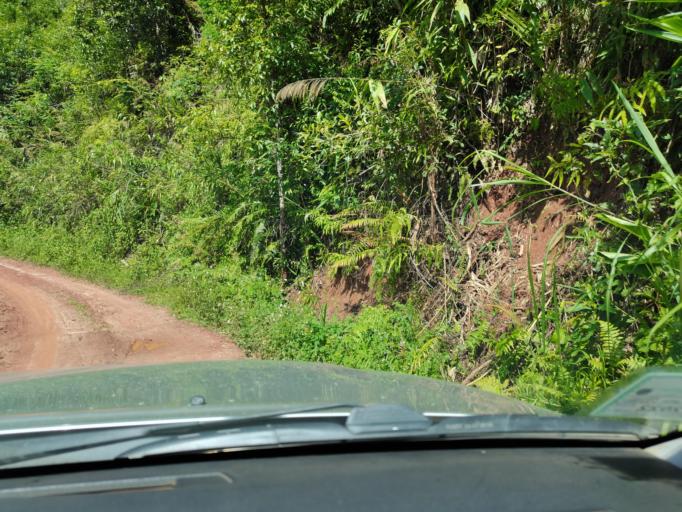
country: LA
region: Loungnamtha
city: Muang Nale
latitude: 20.5511
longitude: 101.0658
